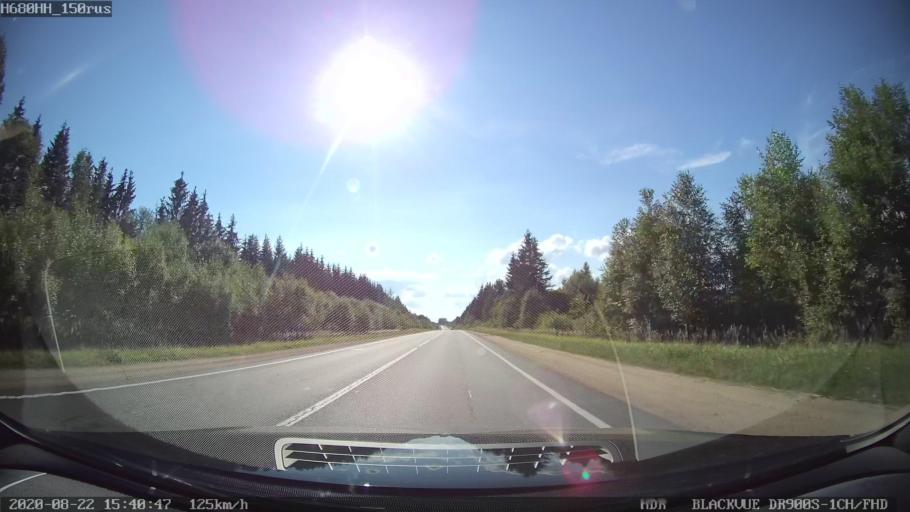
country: RU
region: Tverskaya
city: Bezhetsk
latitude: 57.7531
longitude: 36.5860
